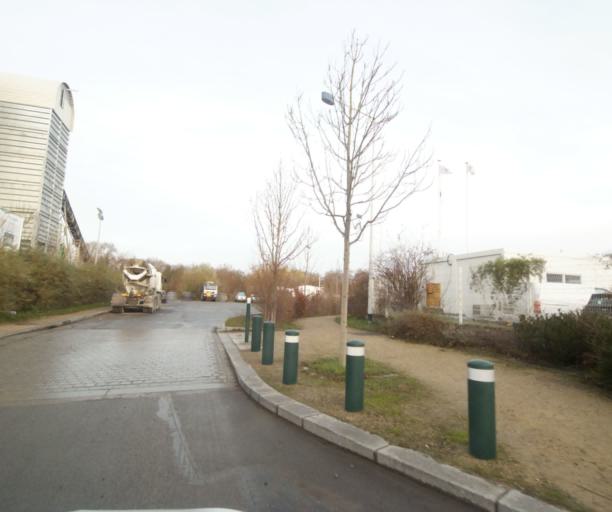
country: FR
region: Ile-de-France
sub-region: Departement des Yvelines
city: Carrieres-sur-Seine
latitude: 48.9007
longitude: 2.1810
